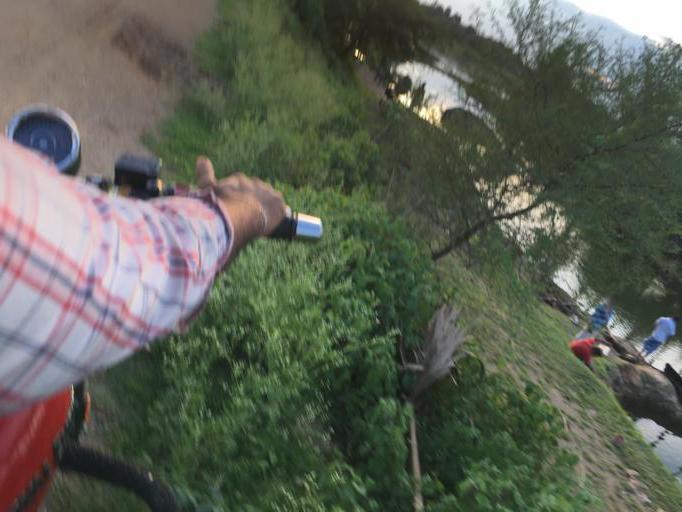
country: IN
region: Telangana
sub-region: Nalgonda
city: Nalgonda
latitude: 17.1763
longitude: 79.4127
